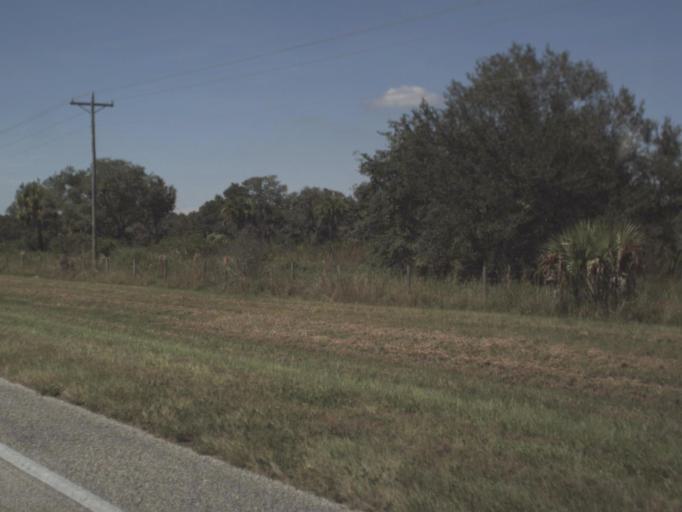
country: US
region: Florida
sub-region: Hendry County
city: Port LaBelle
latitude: 26.9199
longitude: -81.2982
